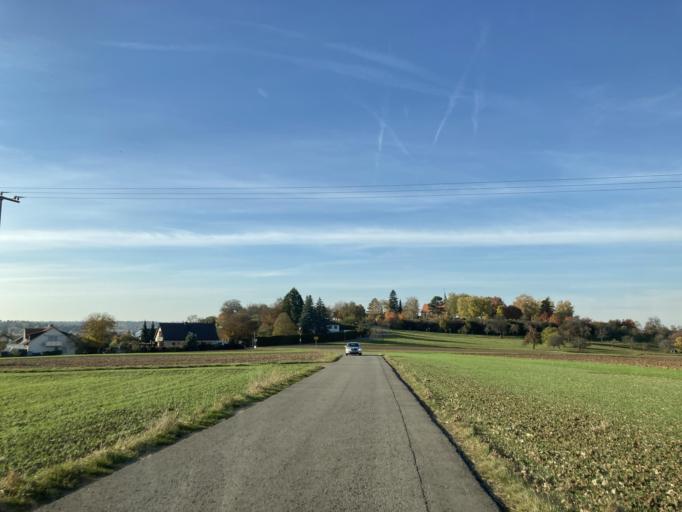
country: DE
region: Baden-Wuerttemberg
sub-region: Tuebingen Region
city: Mossingen
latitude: 48.3930
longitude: 9.0496
